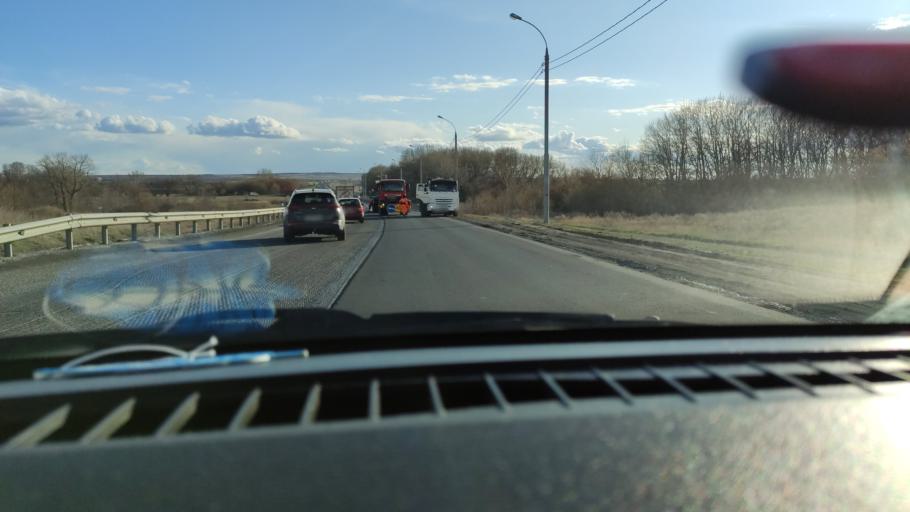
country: RU
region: Saratov
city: Yelshanka
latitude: 51.8248
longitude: 46.2204
